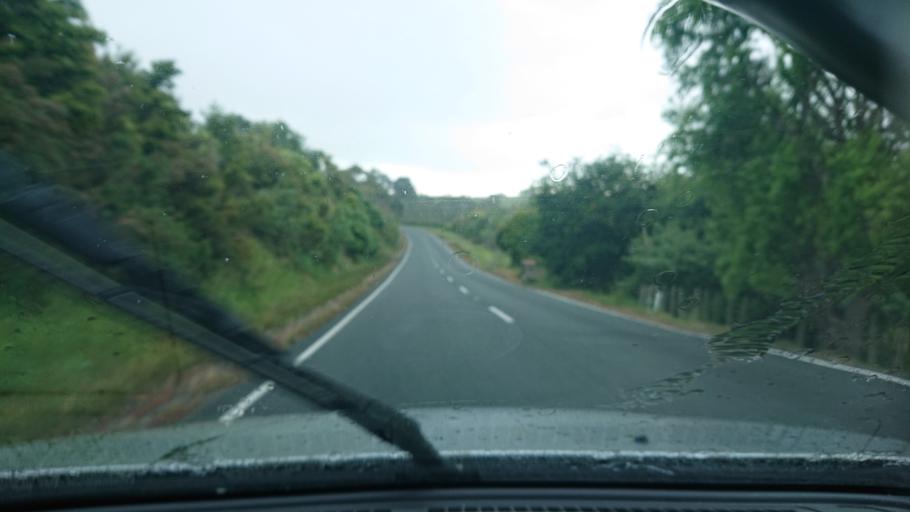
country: NZ
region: Auckland
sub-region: Auckland
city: Wellsford
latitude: -36.3310
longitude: 174.4041
